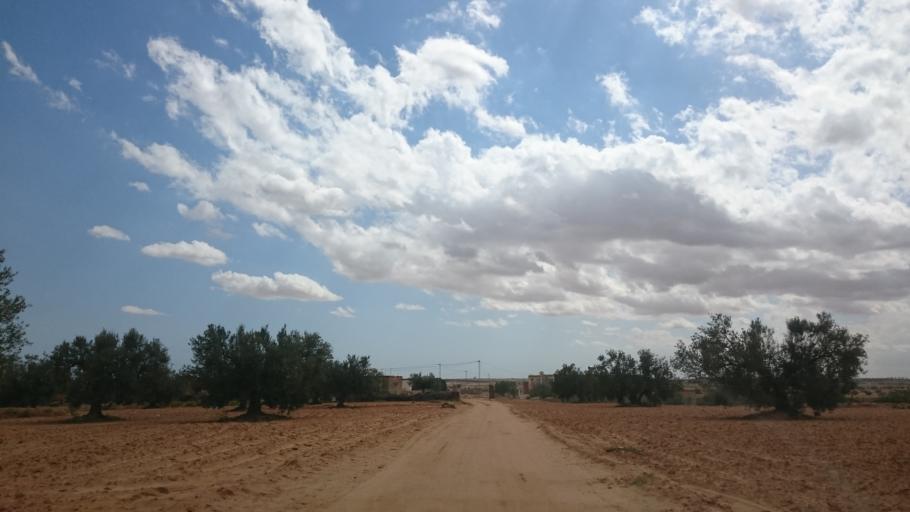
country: TN
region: Safaqis
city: Sfax
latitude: 34.7485
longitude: 10.4863
